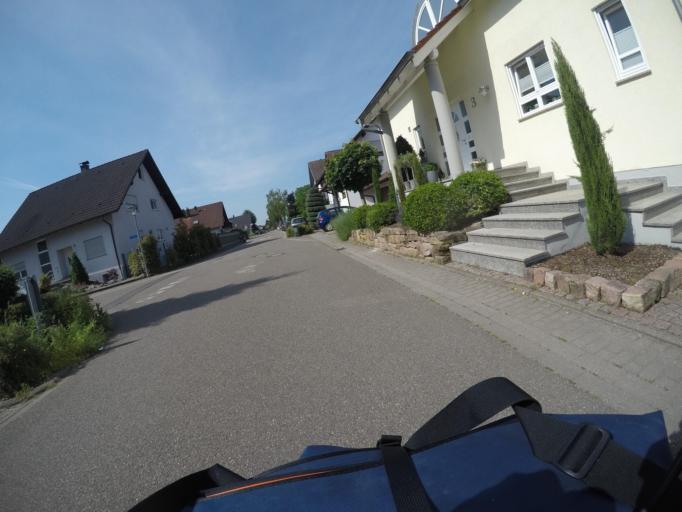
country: DE
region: Baden-Wuerttemberg
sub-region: Karlsruhe Region
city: Otigheim
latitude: 48.8951
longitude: 8.2430
